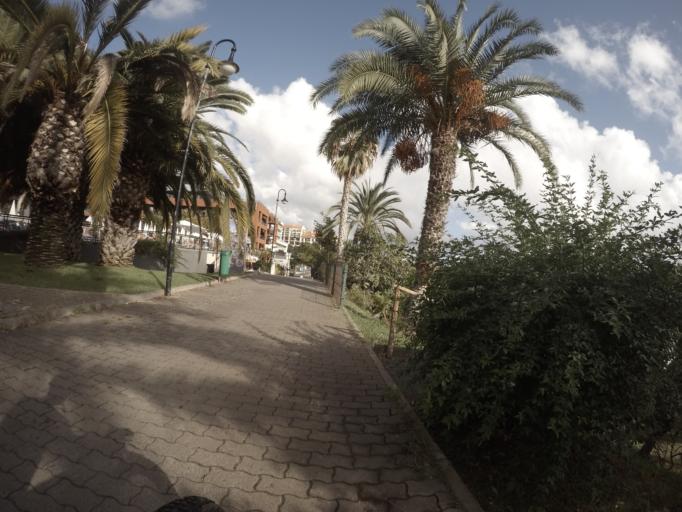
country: PT
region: Madeira
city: Camara de Lobos
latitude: 32.6369
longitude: -16.9360
